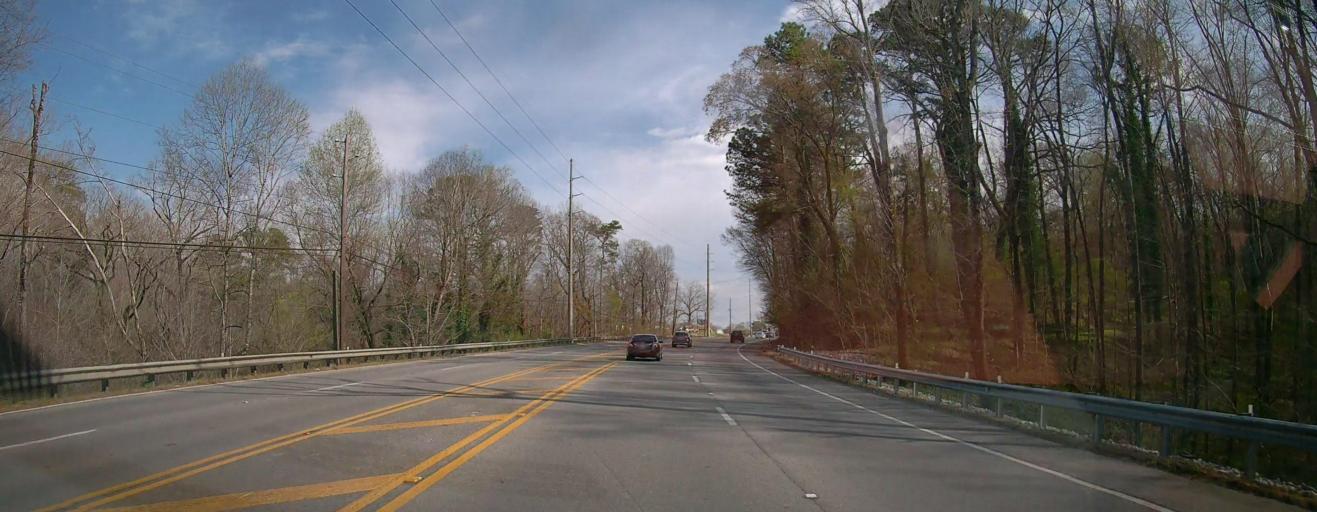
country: US
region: Alabama
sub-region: Jefferson County
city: Forestdale
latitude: 33.5725
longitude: -86.9021
